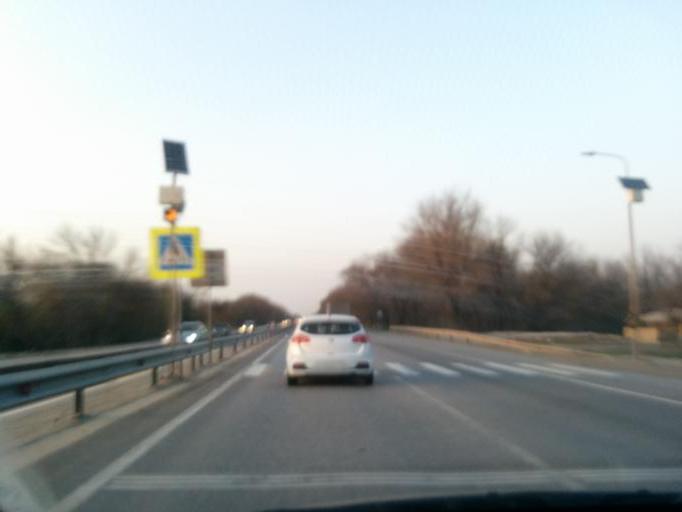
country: RU
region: Rostov
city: Aksay
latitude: 47.3299
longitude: 39.8653
